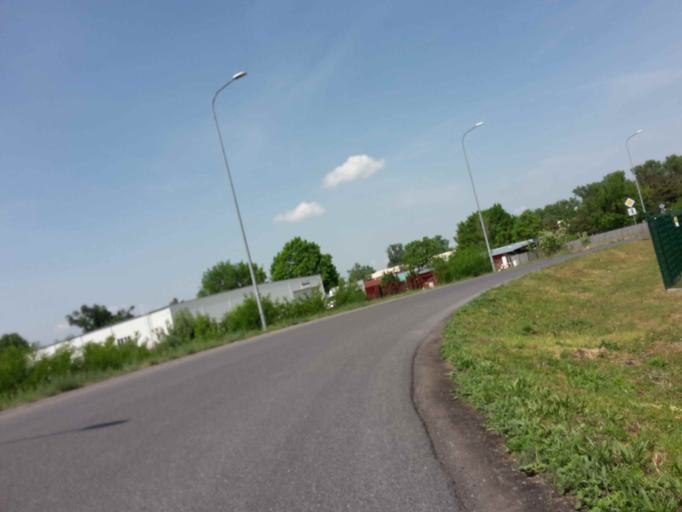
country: SK
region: Bratislavsky
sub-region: Okres Malacky
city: Malacky
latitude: 48.4222
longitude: 17.0272
